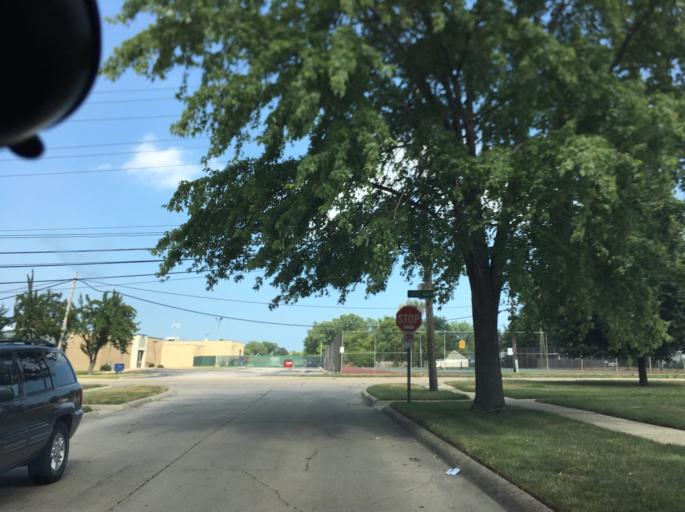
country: US
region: Michigan
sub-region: Macomb County
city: Clinton
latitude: 42.5554
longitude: -82.9108
